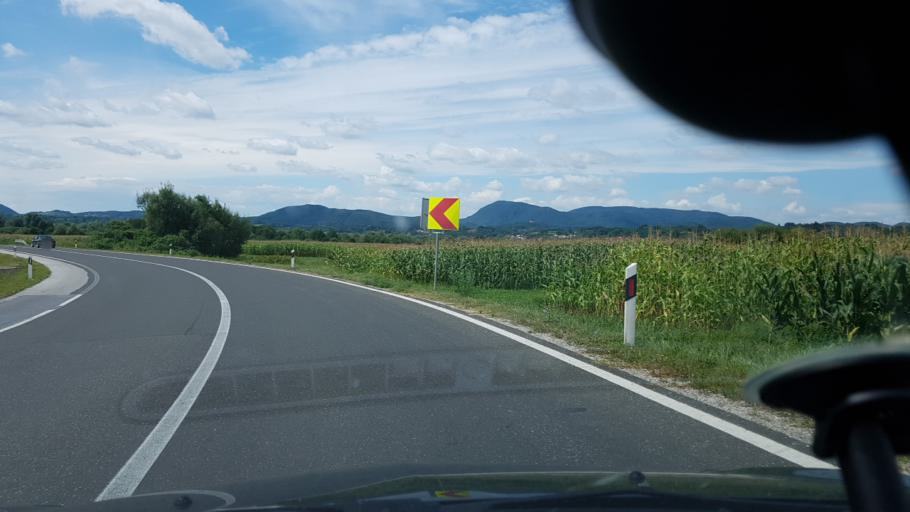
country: HR
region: Varazdinska
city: Ivanec
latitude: 46.2253
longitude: 16.0886
